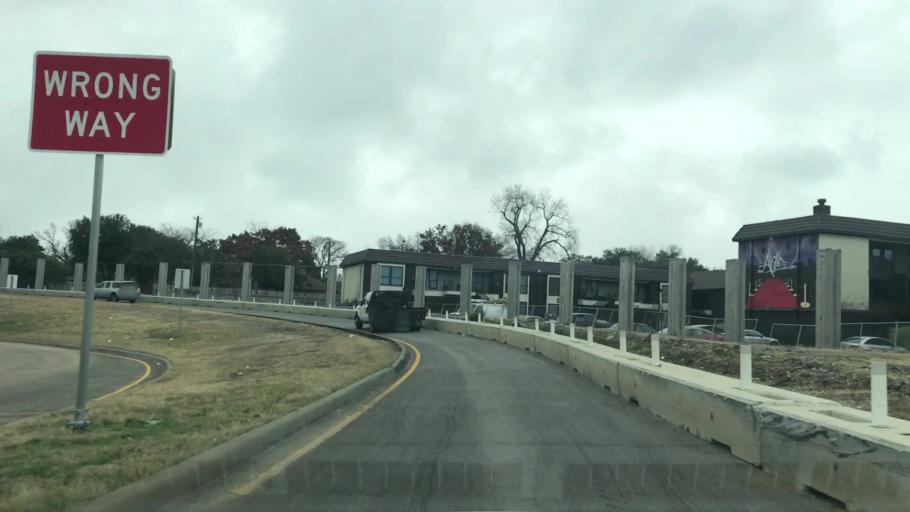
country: US
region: Texas
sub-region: Dallas County
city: Richardson
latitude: 32.8939
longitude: -96.7128
